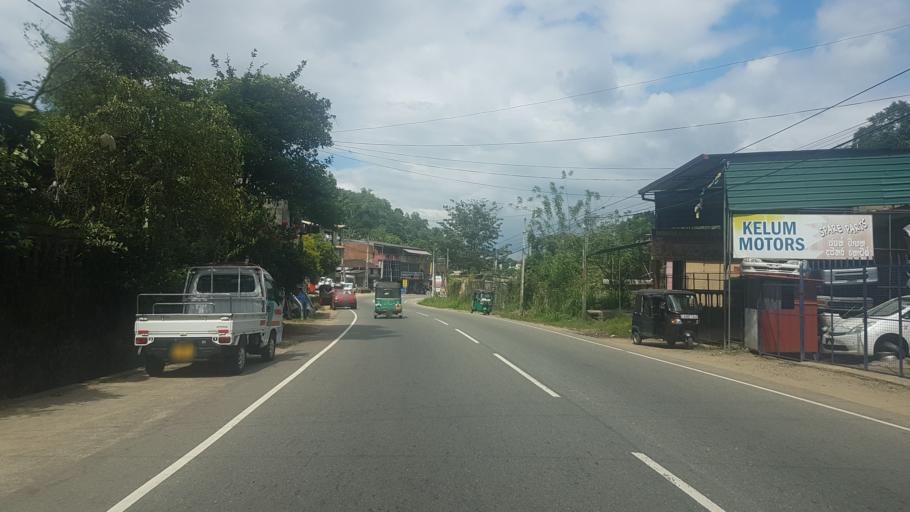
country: LK
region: Central
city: Gampola
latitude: 7.2073
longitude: 80.5991
